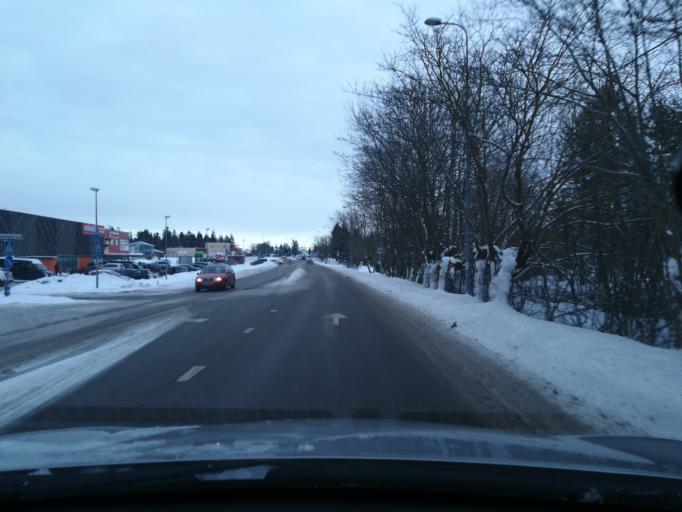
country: EE
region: Harju
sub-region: Harku vald
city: Tabasalu
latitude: 59.4297
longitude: 24.5421
